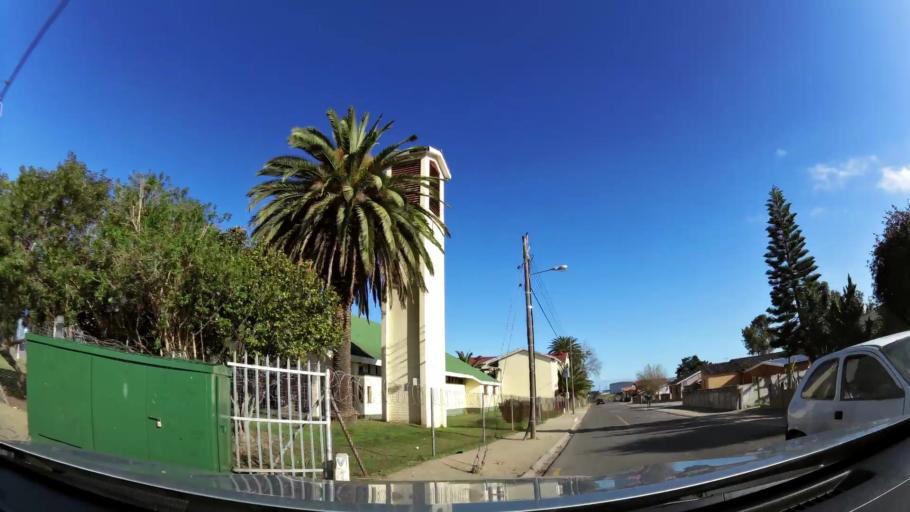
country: ZA
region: Western Cape
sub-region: Eden District Municipality
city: George
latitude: -33.9733
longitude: 22.4782
